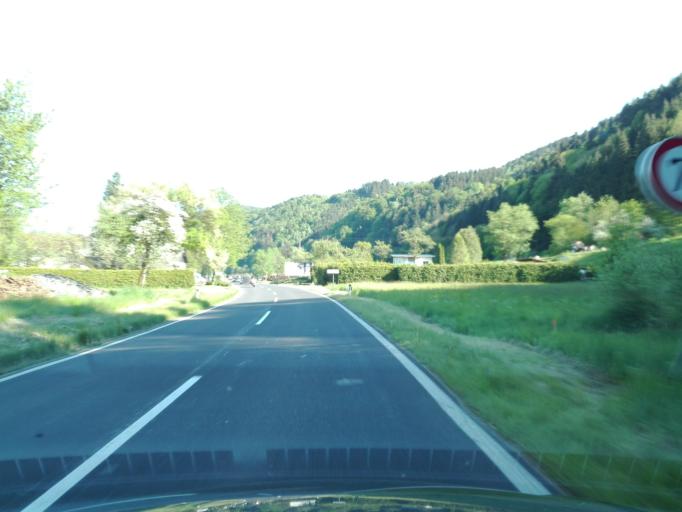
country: AT
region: Upper Austria
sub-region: Politischer Bezirk Rohrbach
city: Pfarrkirchen im Muehlkreis
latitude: 48.4728
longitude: 13.7718
